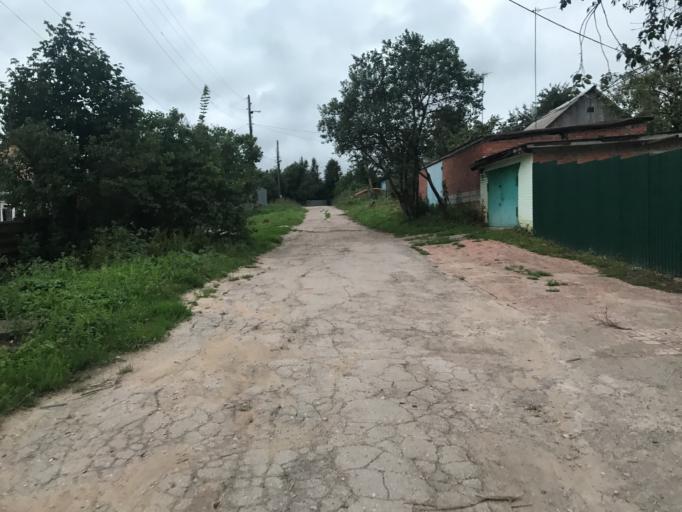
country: RU
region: Tula
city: Priupskiy
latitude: 53.9370
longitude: 37.7109
